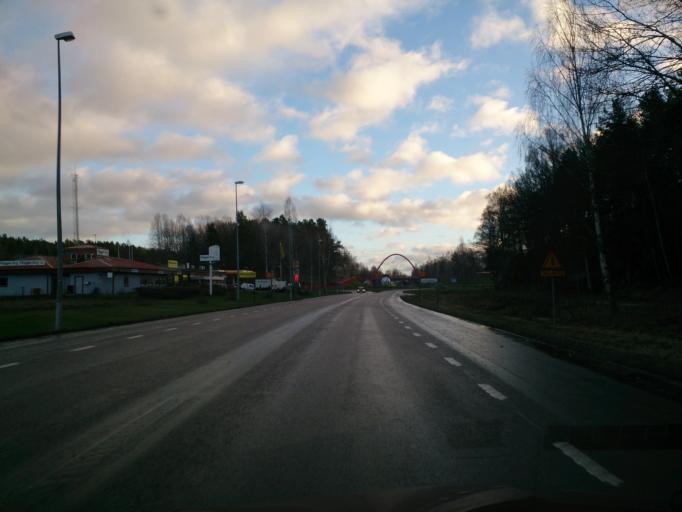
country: SE
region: OEstergoetland
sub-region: Atvidabergs Kommun
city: Atvidaberg
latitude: 58.2106
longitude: 15.9870
